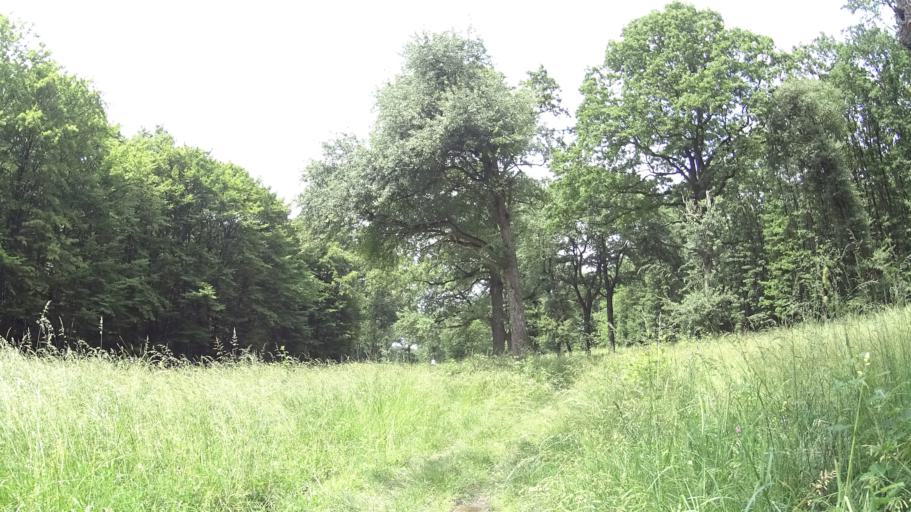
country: HU
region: Pest
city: Nagymaros
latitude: 47.8067
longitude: 18.9416
